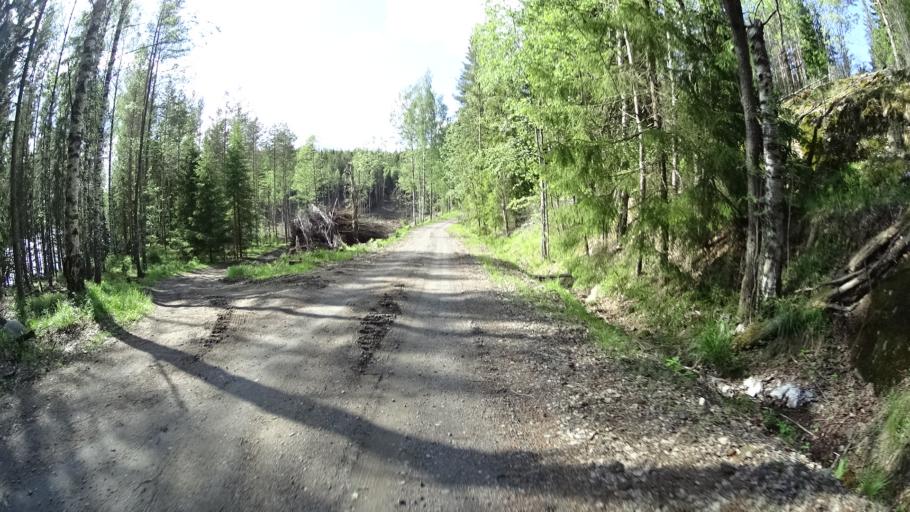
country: FI
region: Varsinais-Suomi
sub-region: Salo
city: Kisko
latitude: 60.1830
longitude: 23.4983
